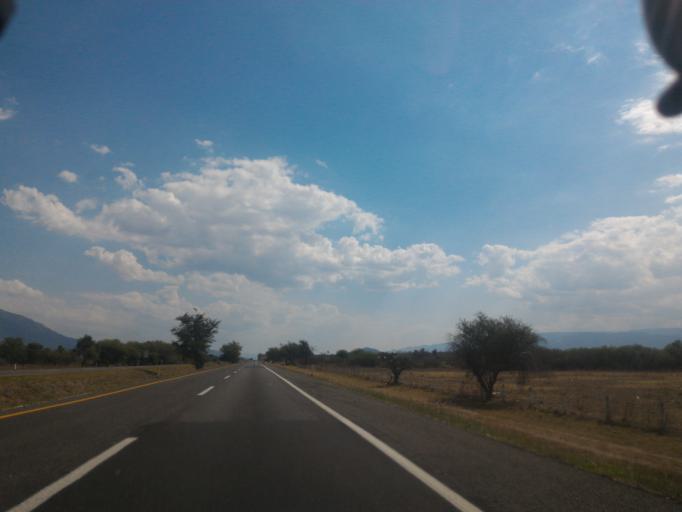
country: MX
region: Jalisco
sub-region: Acatlan de Juarez
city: Villa de los Ninos
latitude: 20.3463
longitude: -103.5740
